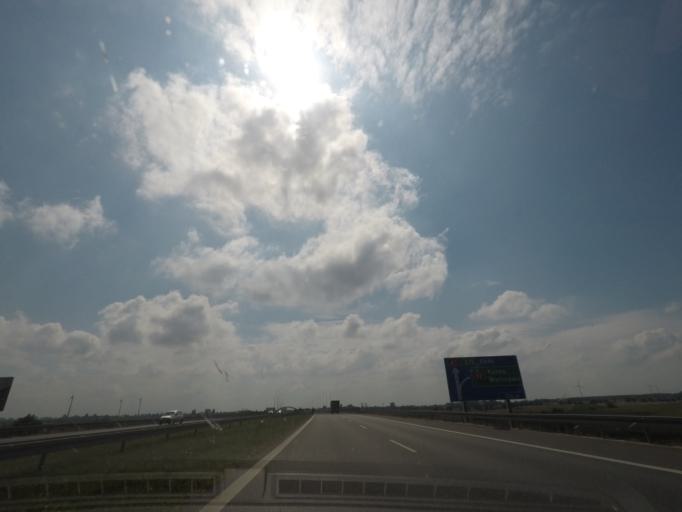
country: PL
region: Lodz Voivodeship
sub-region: Powiat kutnowski
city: Krzyzanow
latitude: 52.2313
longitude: 19.4576
